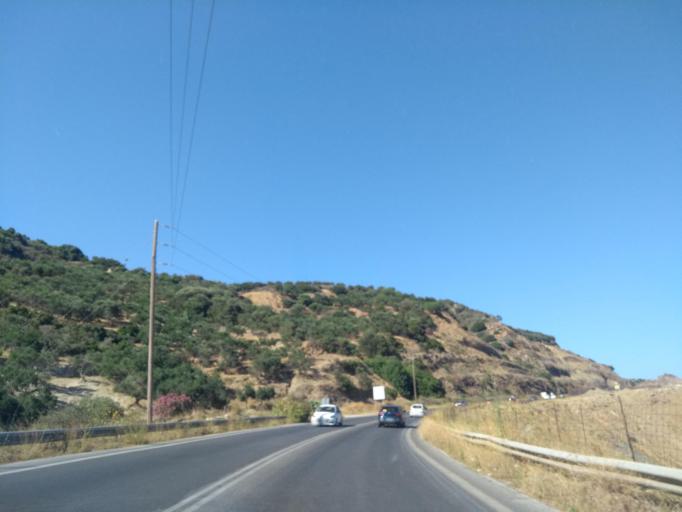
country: GR
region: Crete
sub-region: Nomos Chanias
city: Kolympari
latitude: 35.5127
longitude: 23.7329
